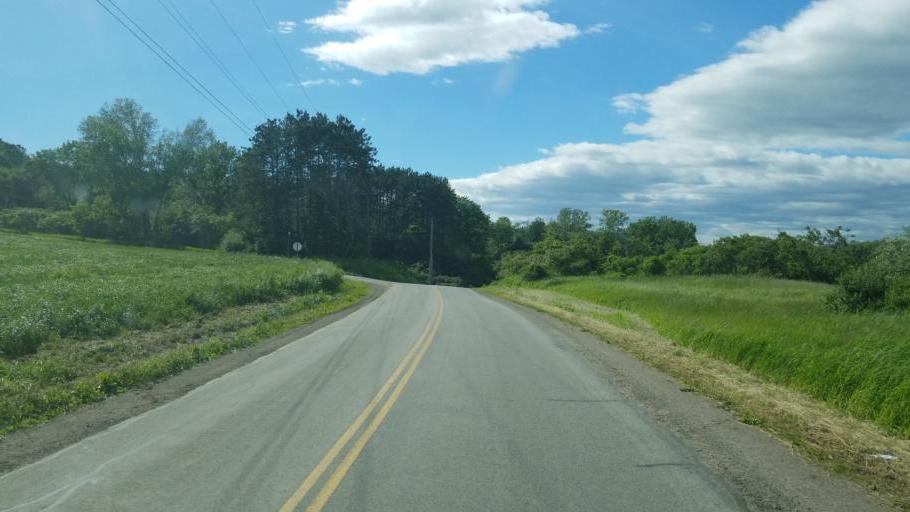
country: US
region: New York
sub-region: Montgomery County
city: Fort Plain
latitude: 42.9644
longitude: -74.6430
